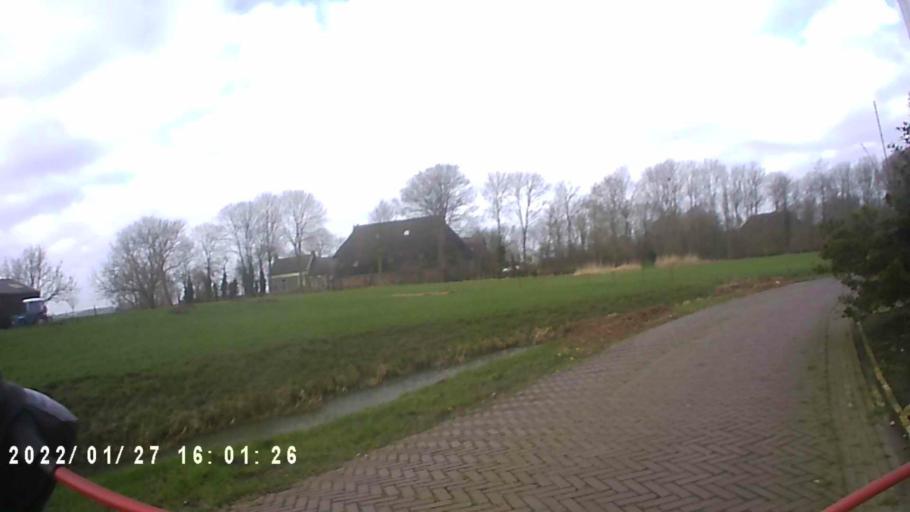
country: NL
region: Friesland
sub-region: Gemeente Dongeradeel
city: Anjum
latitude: 53.3731
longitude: 6.0878
